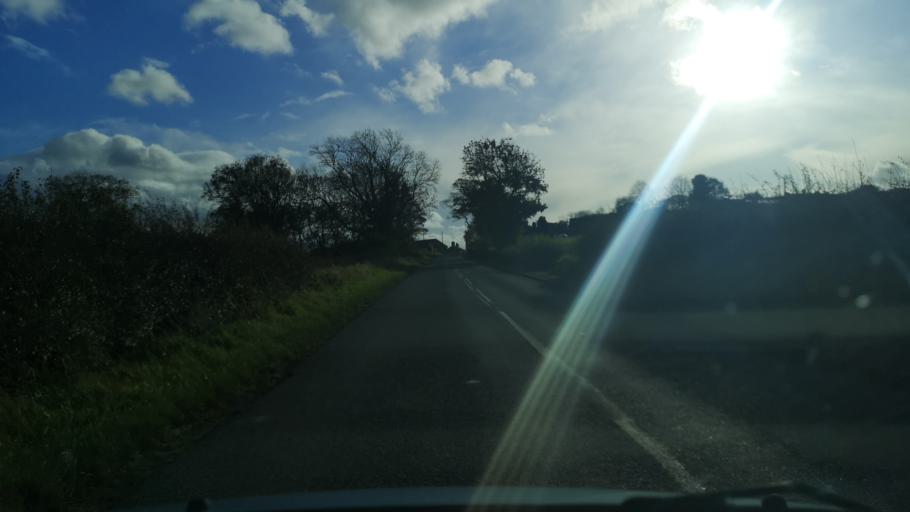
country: GB
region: England
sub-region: City and Borough of Wakefield
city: Middlestown
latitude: 53.6362
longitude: -1.6231
